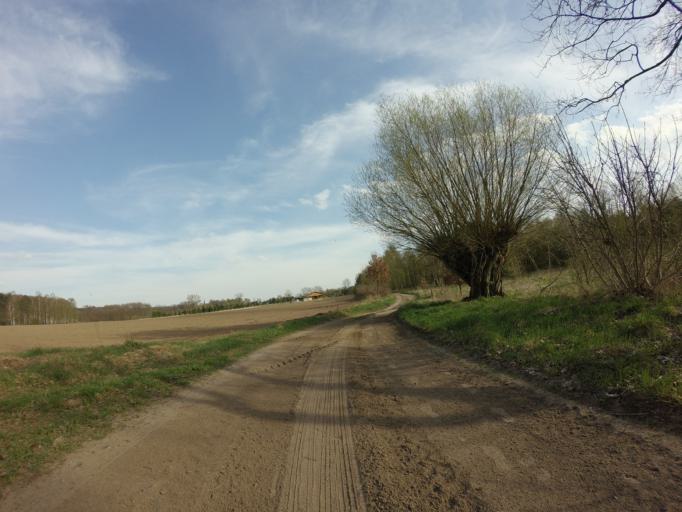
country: PL
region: West Pomeranian Voivodeship
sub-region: Powiat choszczenski
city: Choszczno
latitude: 53.1944
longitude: 15.4982
